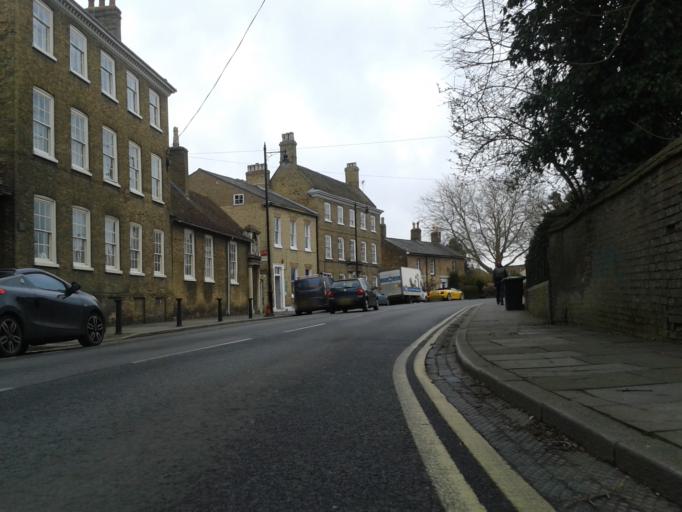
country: GB
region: England
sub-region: Cambridgeshire
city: Ely
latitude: 52.3997
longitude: 0.2603
